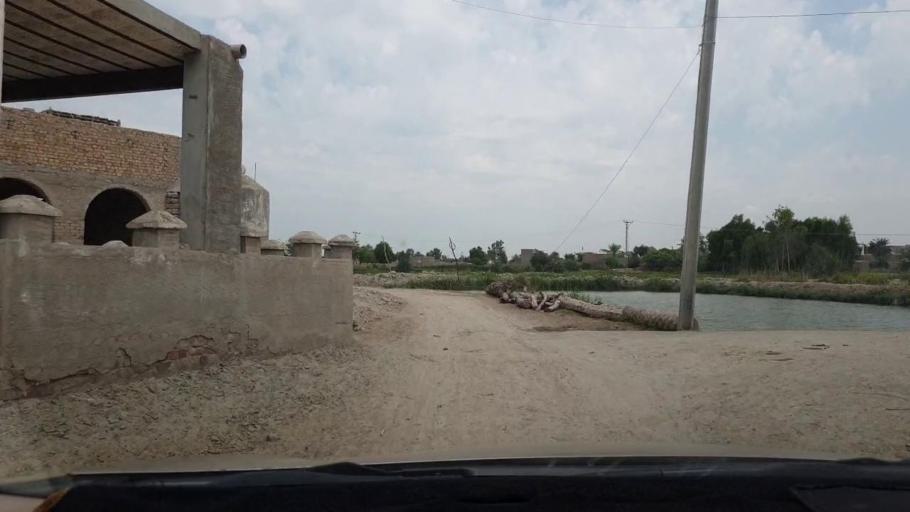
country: PK
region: Sindh
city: Naudero
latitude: 27.7244
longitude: 68.3389
